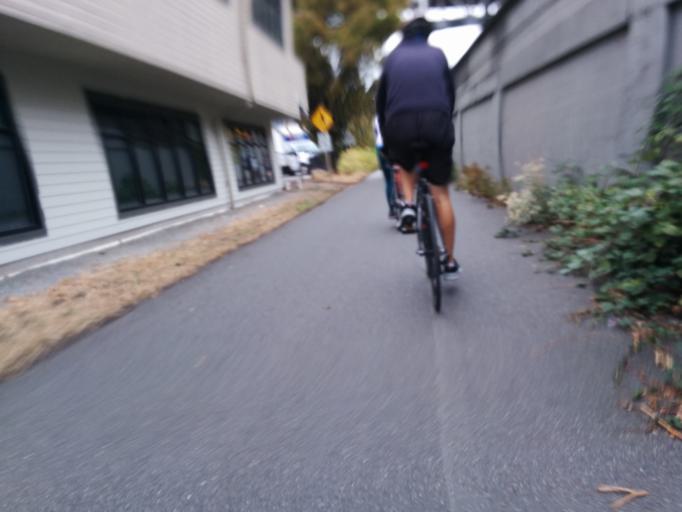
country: US
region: Washington
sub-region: King County
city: Seattle
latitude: 47.6488
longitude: -122.3450
